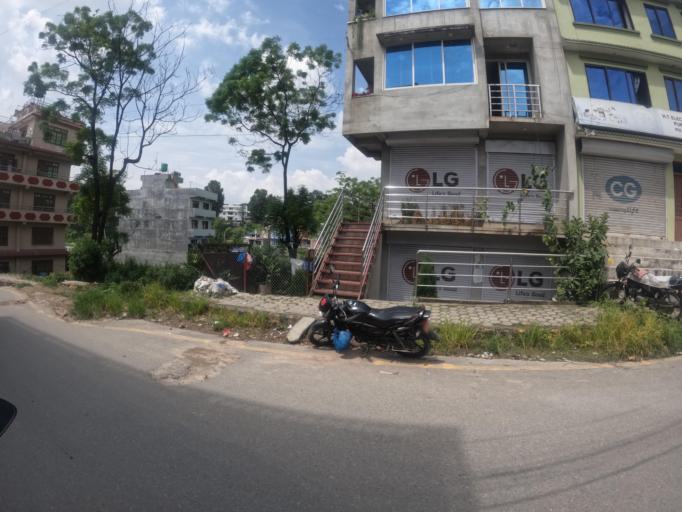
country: NP
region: Central Region
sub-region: Bagmati Zone
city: Bhaktapur
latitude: 27.6812
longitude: 85.3829
